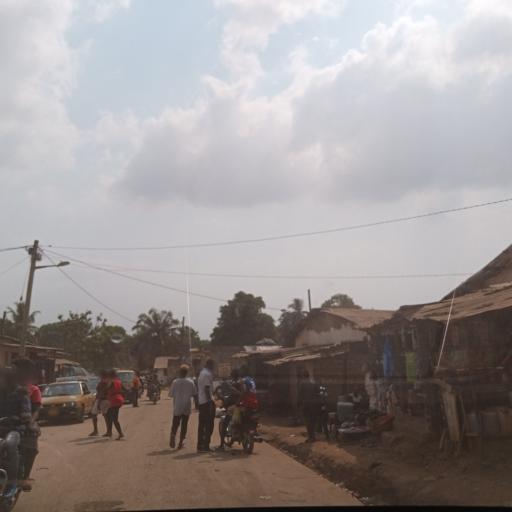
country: LR
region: Montserrado
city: Monrovia
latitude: 6.2901
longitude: -10.6899
